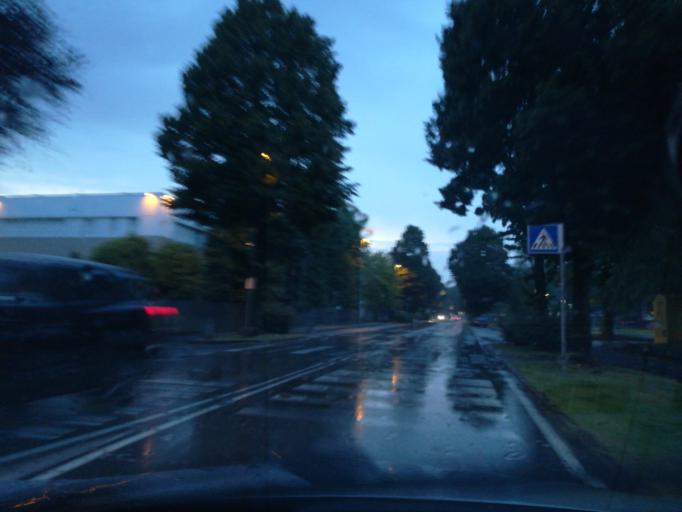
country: IT
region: Lombardy
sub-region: Provincia di Bergamo
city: Brembate di Sopra
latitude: 45.7174
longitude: 9.5817
